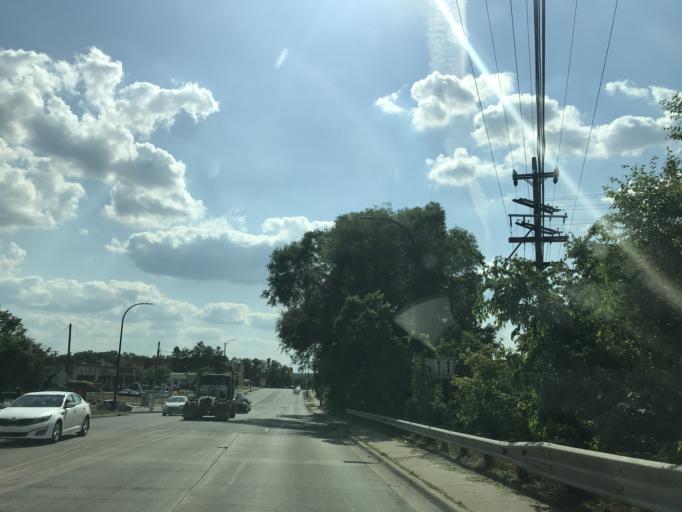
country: US
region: Michigan
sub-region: Washtenaw County
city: Ypsilanti
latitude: 42.2419
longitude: -83.5988
